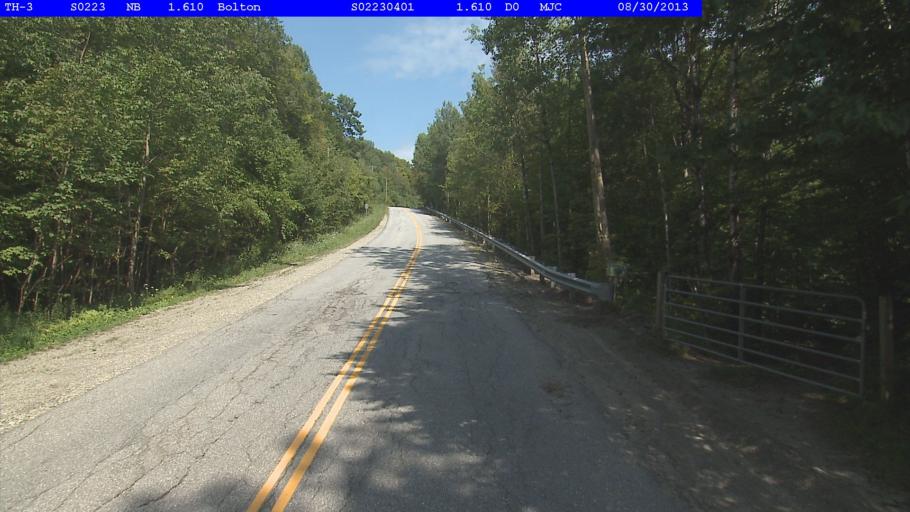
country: US
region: Vermont
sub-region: Washington County
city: Waterbury
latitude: 44.3932
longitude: -72.8765
